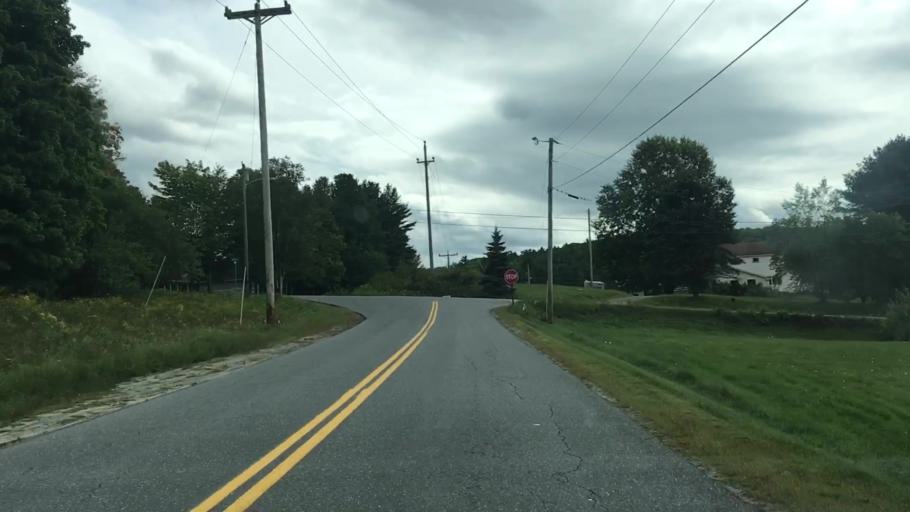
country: US
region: Maine
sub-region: Kennebec County
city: Hallowell
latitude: 44.2655
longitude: -69.8142
